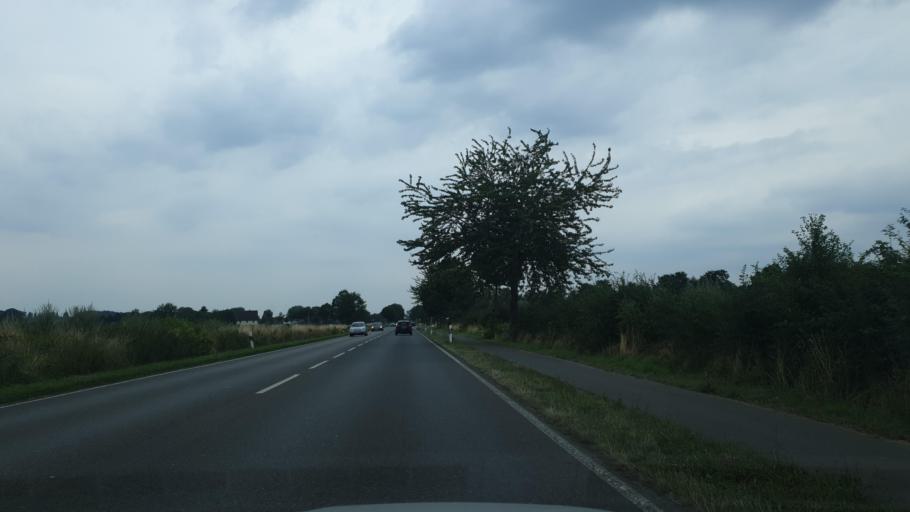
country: DE
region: North Rhine-Westphalia
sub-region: Regierungsbezirk Detmold
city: Bad Salzuflen
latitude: 52.0713
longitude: 8.7353
